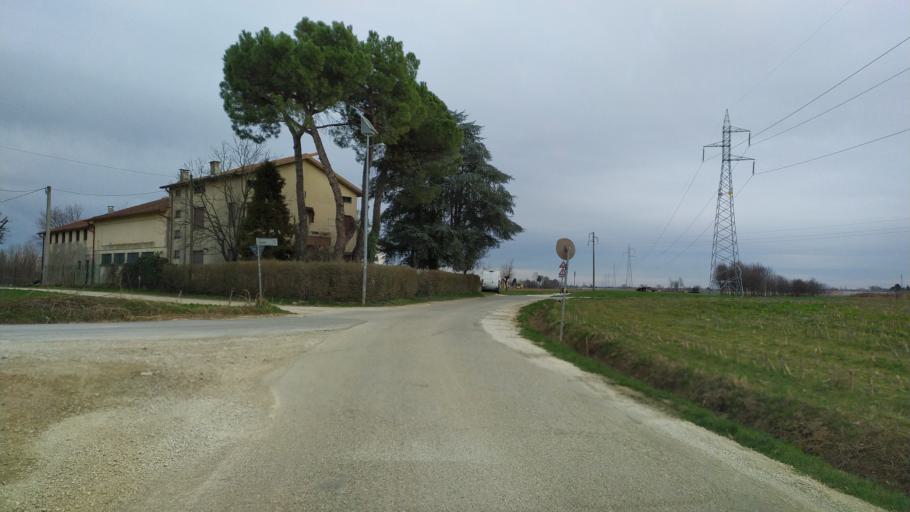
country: IT
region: Veneto
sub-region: Provincia di Vicenza
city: Malo
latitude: 45.6562
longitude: 11.4348
